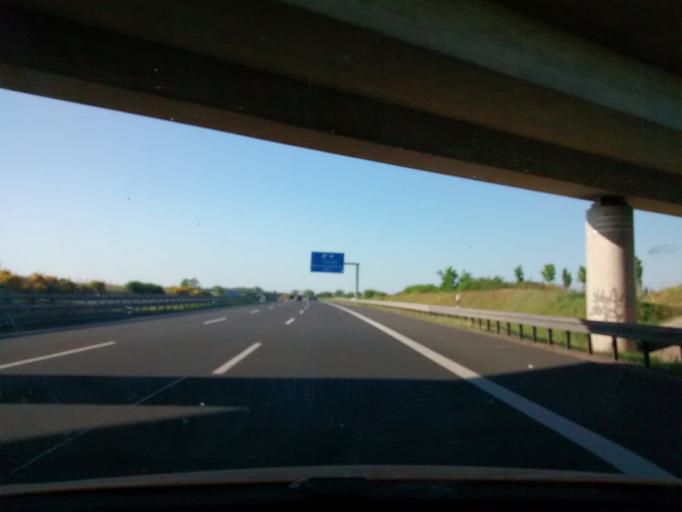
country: DE
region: Brandenburg
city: Schulzendorf
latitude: 52.3644
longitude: 13.5485
